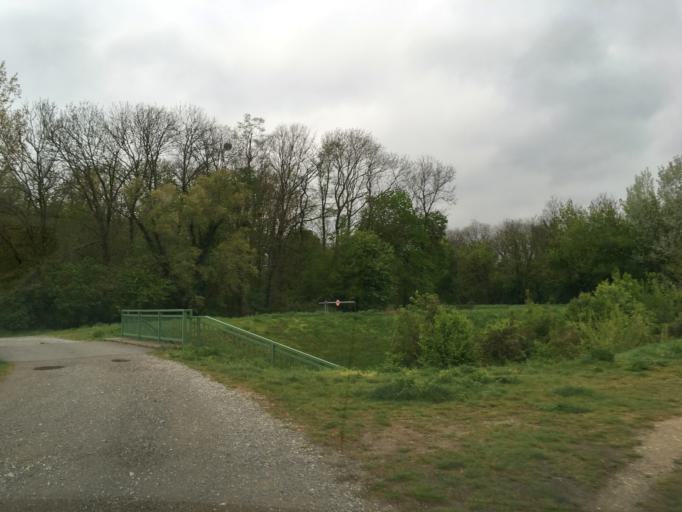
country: AT
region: Lower Austria
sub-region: Politischer Bezirk Bruck an der Leitha
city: Bruck an der Leitha
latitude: 48.0155
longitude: 16.7671
